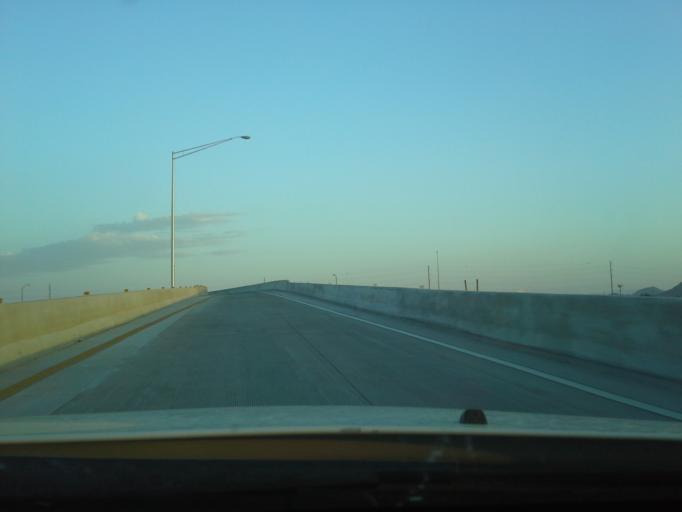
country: US
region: Arizona
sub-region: Maricopa County
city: Paradise Valley
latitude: 33.6747
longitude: -112.0052
